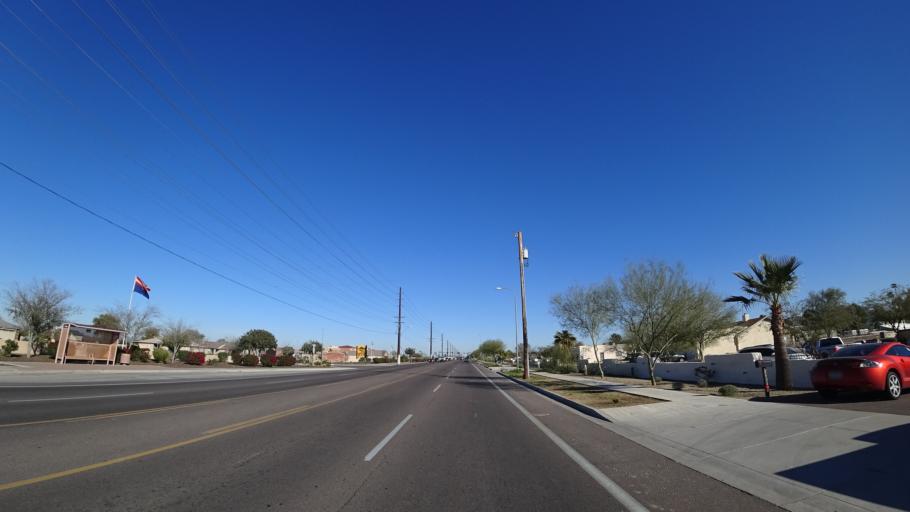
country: US
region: Arizona
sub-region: Maricopa County
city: Laveen
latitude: 33.3921
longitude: -112.1201
